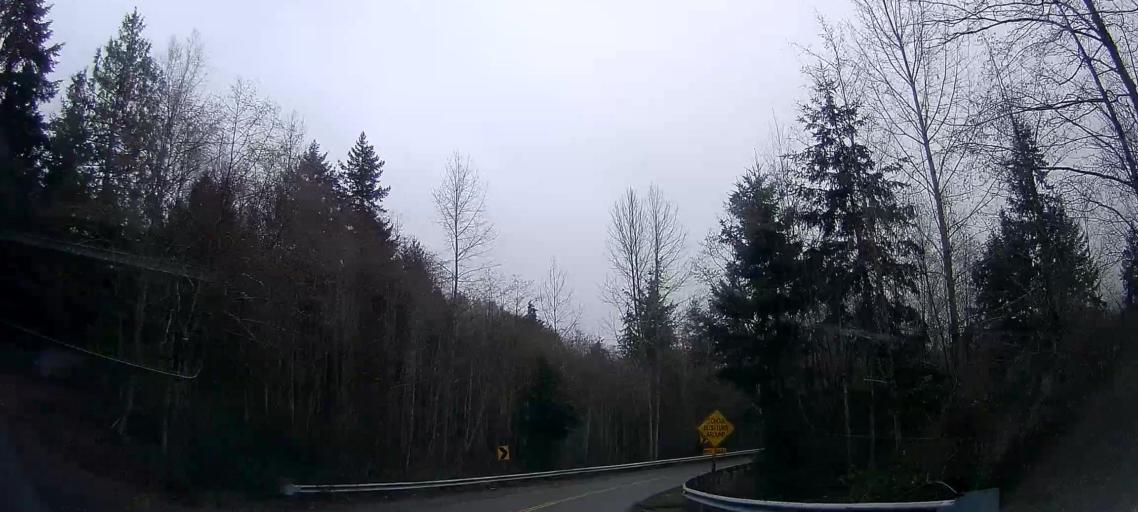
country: US
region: Washington
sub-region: Skagit County
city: Mount Vernon
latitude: 48.3761
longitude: -122.2996
